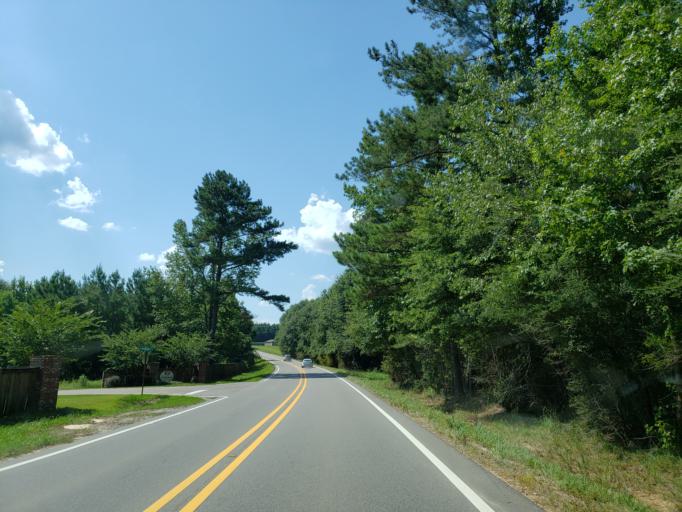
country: US
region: Mississippi
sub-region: Lamar County
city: Sumrall
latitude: 31.3837
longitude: -89.5273
